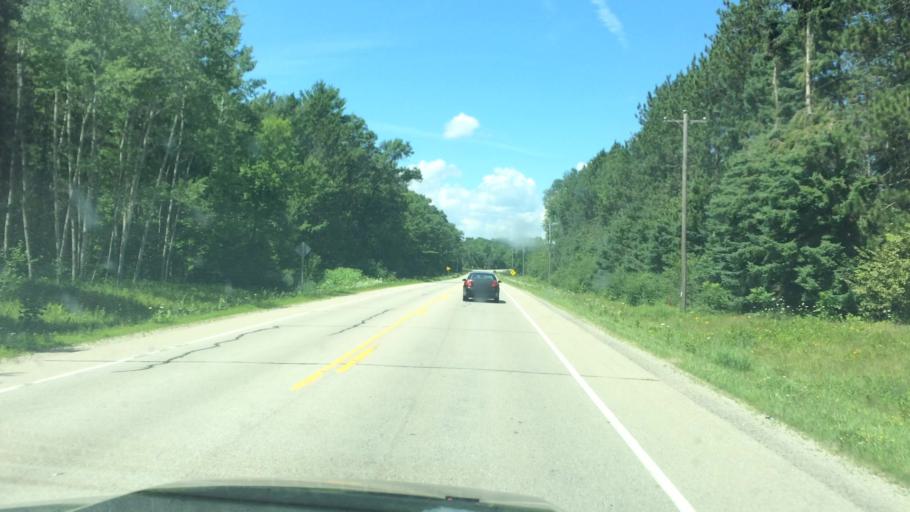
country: US
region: Wisconsin
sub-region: Marinette County
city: Peshtigo
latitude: 45.1003
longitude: -87.7359
